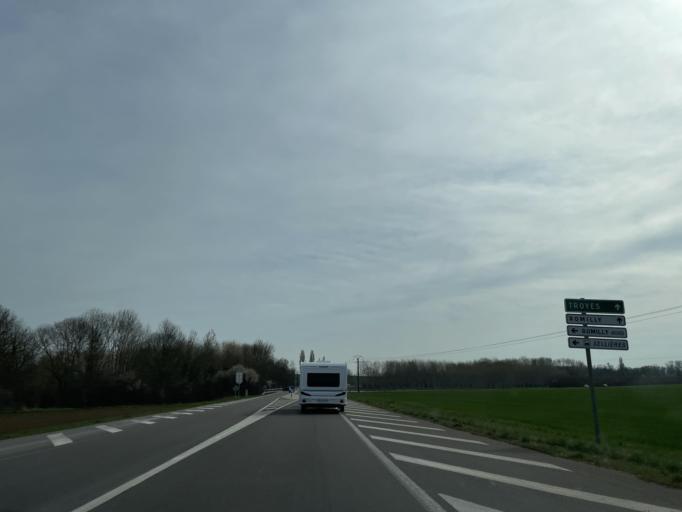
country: FR
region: Champagne-Ardenne
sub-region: Departement de l'Aube
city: Romilly-sur-Seine
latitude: 48.5130
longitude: 3.6787
